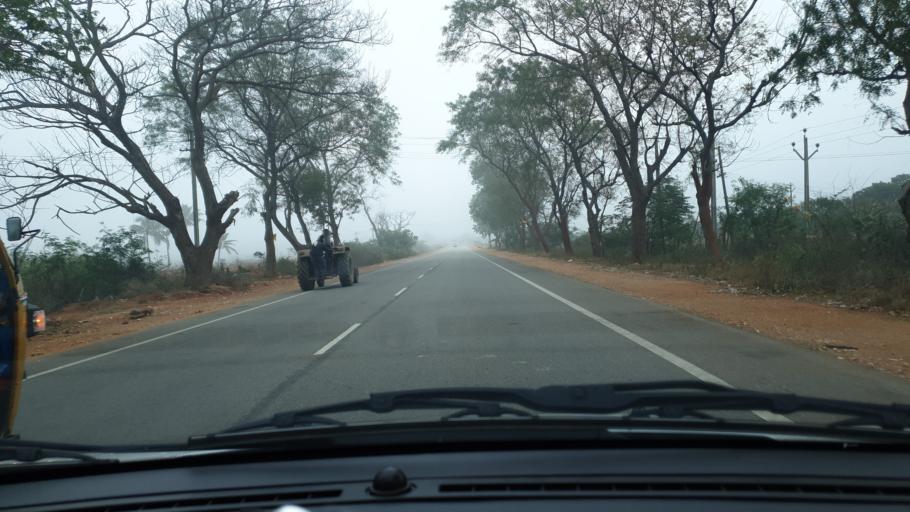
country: IN
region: Telangana
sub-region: Mahbubnagar
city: Nagar Karnul
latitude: 16.6332
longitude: 78.6052
